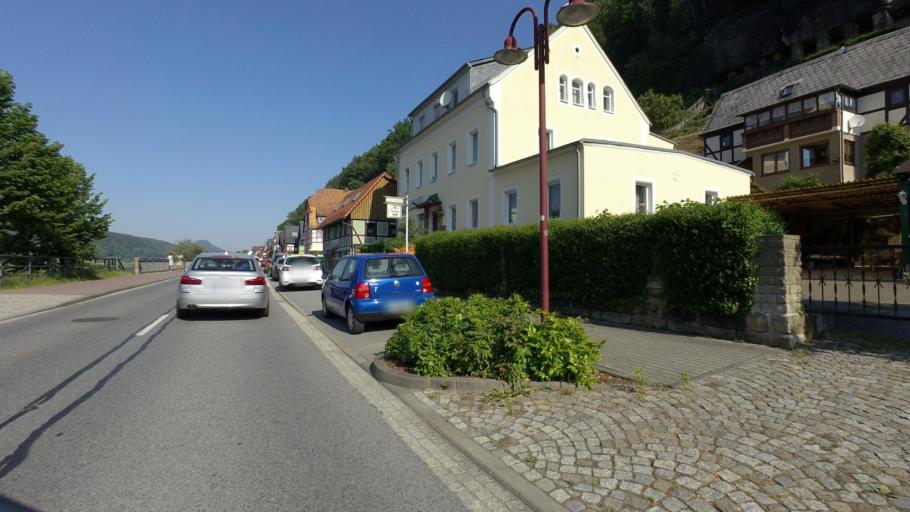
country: DE
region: Saxony
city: Bad Schandau
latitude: 50.9121
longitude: 14.1776
